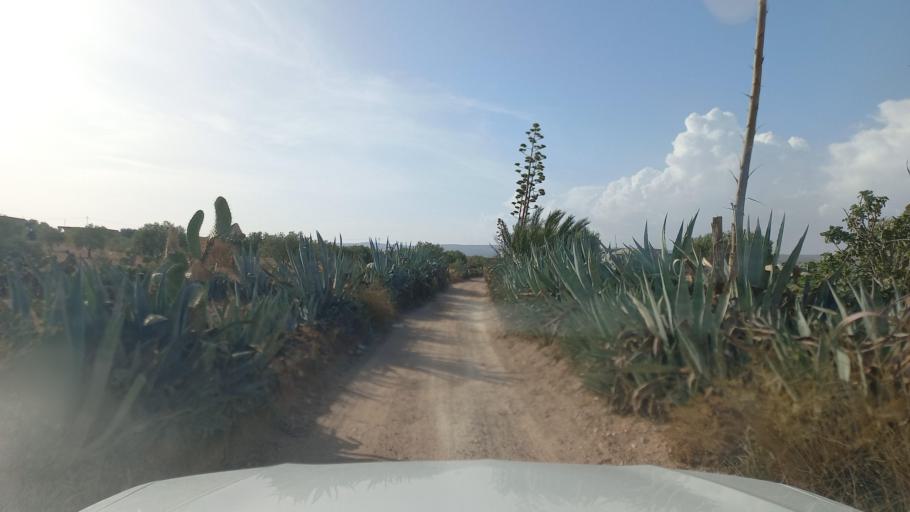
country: TN
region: Al Qasrayn
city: Kasserine
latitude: 35.2289
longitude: 8.9285
